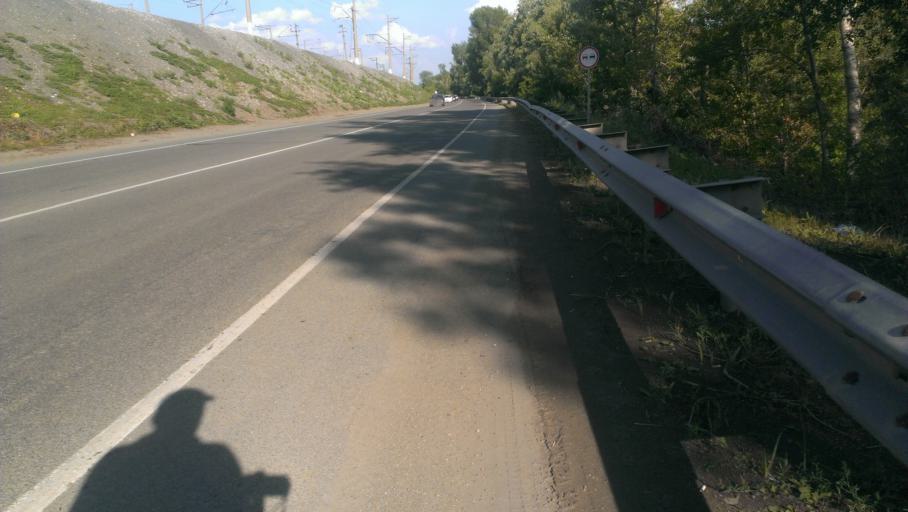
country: RU
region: Altai Krai
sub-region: Gorod Barnaulskiy
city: Barnaul
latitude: 53.3674
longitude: 83.8347
